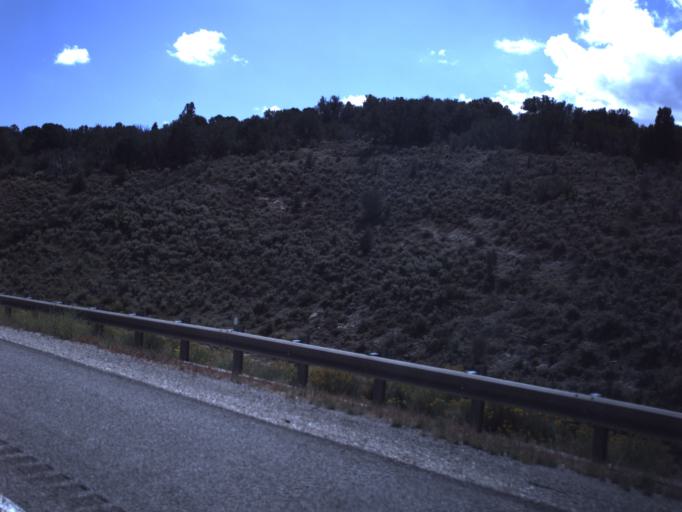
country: US
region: Utah
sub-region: Wayne County
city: Loa
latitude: 38.7785
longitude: -111.4827
